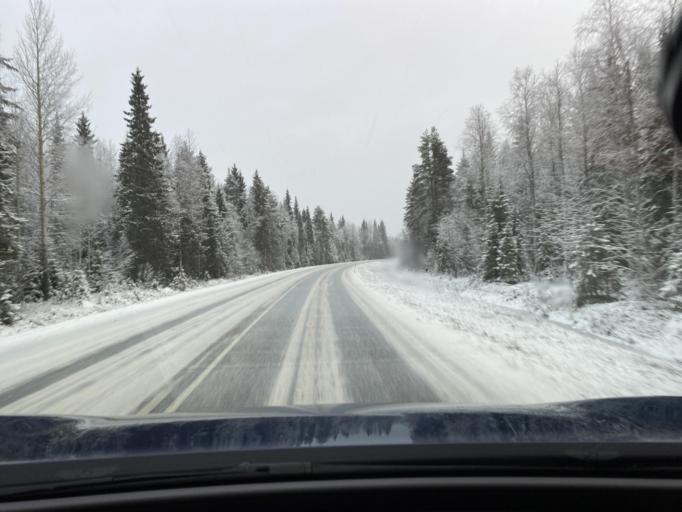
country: FI
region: Lapland
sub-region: Rovaniemi
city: Rovaniemi
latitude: 65.9606
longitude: 25.9462
